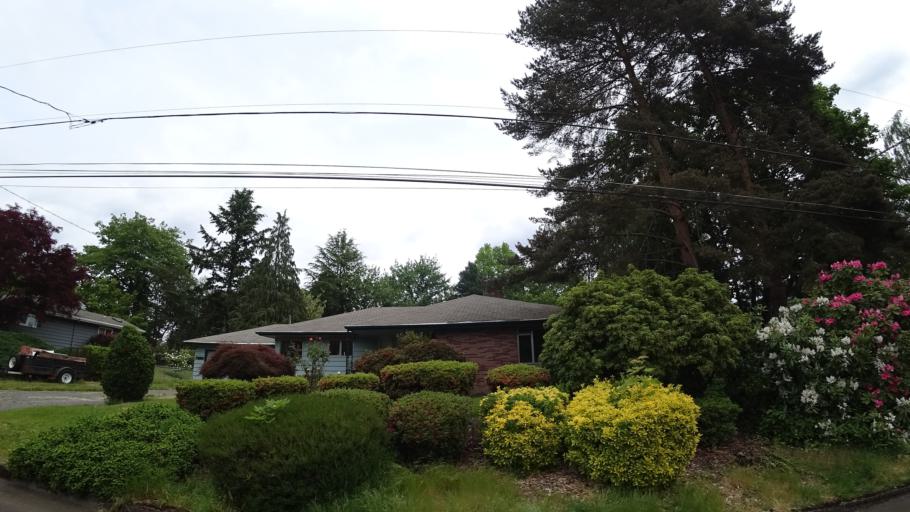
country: US
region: Oregon
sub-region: Washington County
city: Garden Home-Whitford
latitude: 45.4633
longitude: -122.7636
